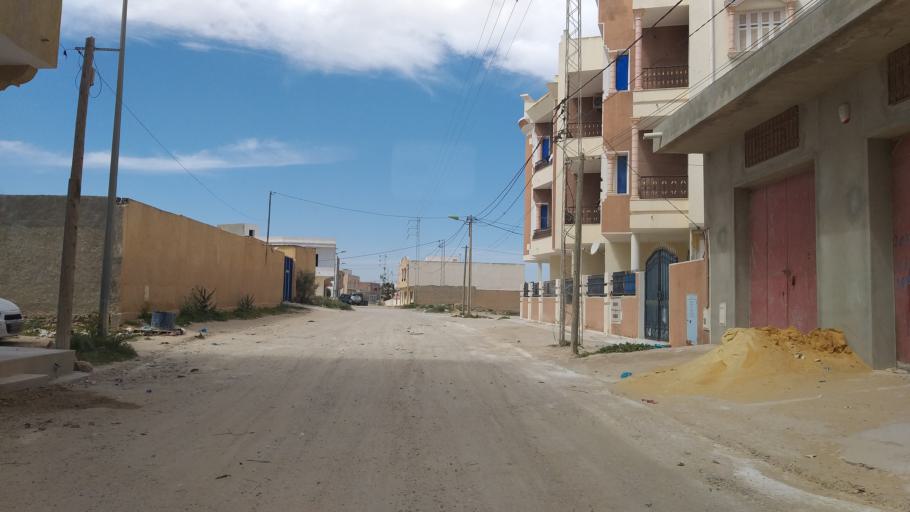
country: TN
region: Al Mahdiyah
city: El Jem
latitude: 35.3027
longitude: 10.6970
